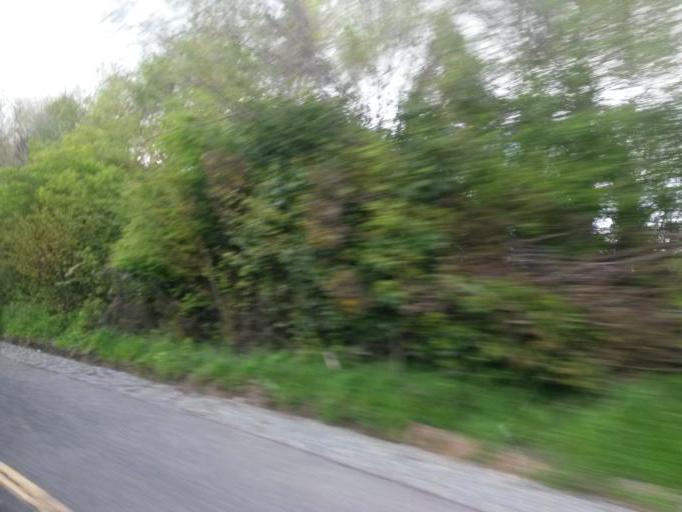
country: IE
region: Leinster
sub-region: Loch Garman
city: Castlebridge
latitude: 52.4089
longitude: -6.5213
